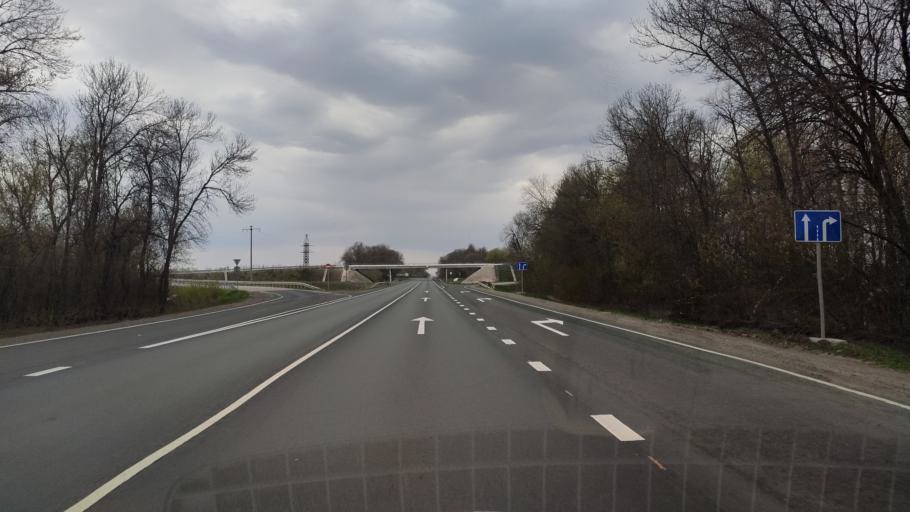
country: RU
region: Voronezj
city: Latnaya
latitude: 51.6204
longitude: 38.6315
